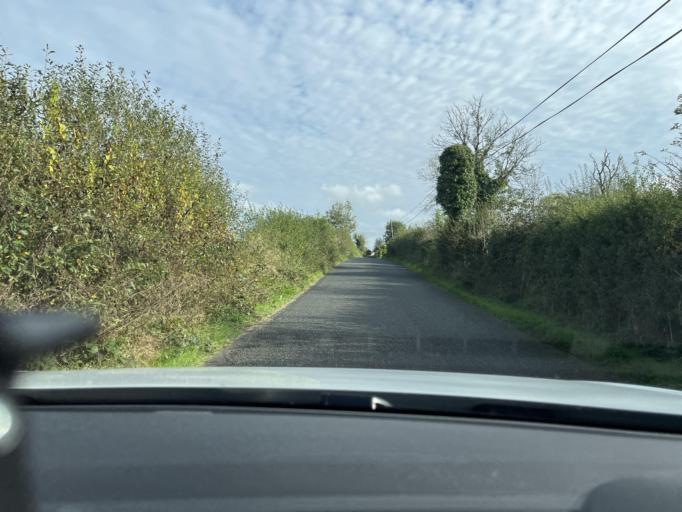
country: IE
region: Connaught
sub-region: Sligo
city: Ballymote
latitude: 54.0803
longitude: -8.4187
